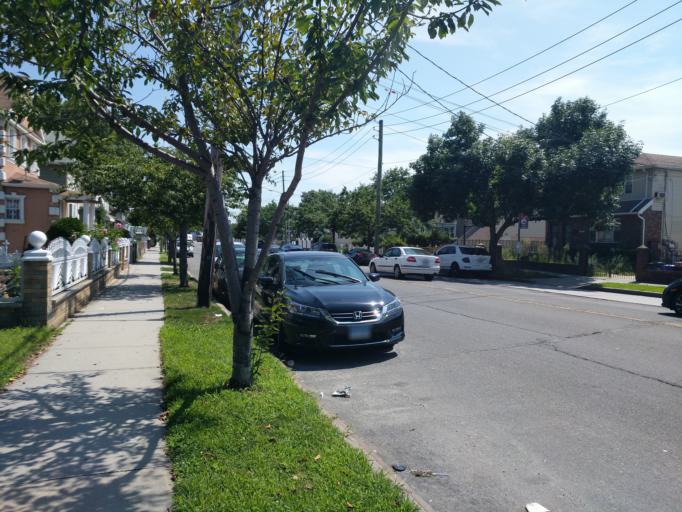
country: US
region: New York
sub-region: Queens County
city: Jamaica
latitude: 40.6659
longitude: -73.7698
